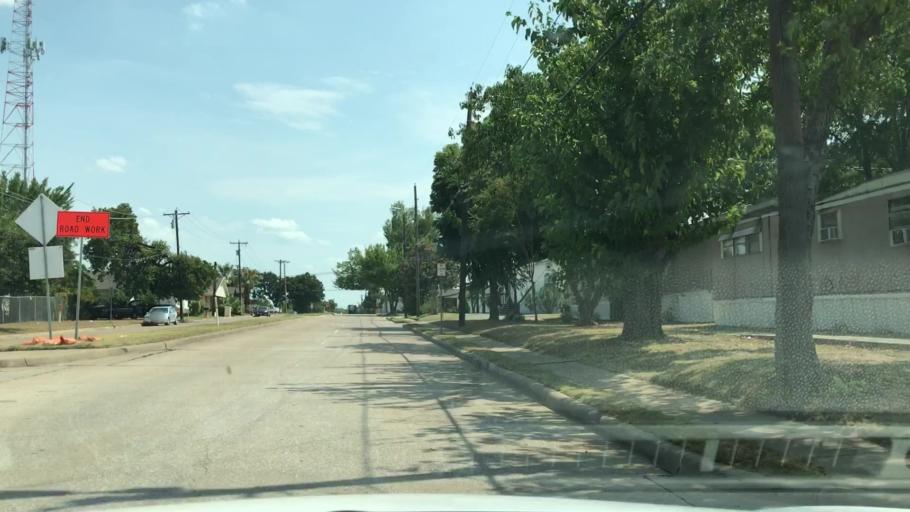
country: US
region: Texas
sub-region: Dallas County
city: Irving
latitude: 32.8327
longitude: -96.9076
